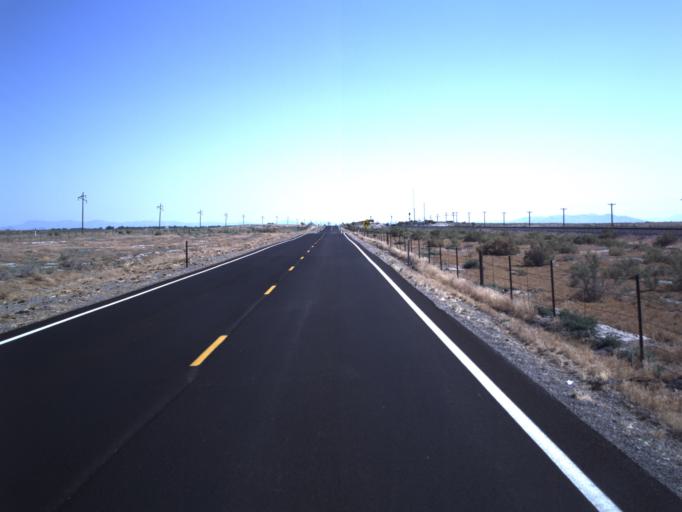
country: US
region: Utah
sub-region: Millard County
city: Delta
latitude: 39.2227
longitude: -112.6739
